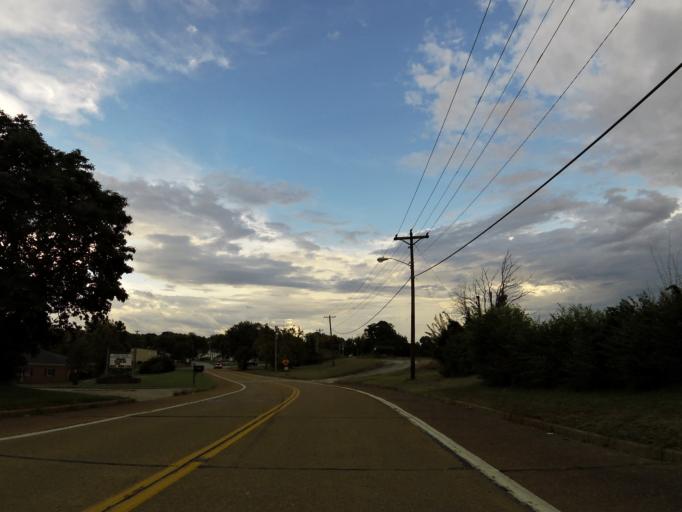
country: US
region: Tennessee
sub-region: Blount County
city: Maryville
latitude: 35.7721
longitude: -83.9673
